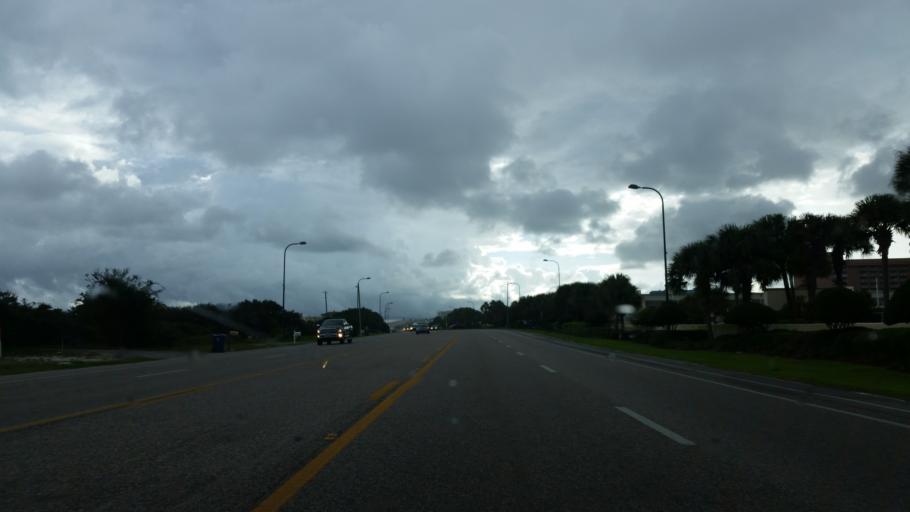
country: US
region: Alabama
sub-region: Baldwin County
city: Orange Beach
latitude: 30.2742
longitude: -87.5658
